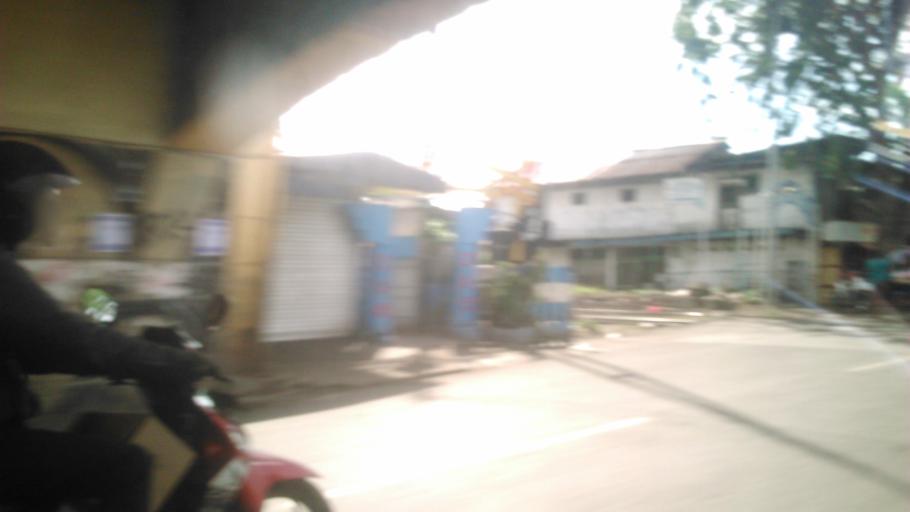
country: ID
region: East Java
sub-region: Kota Surabaya
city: Surabaya
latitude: -7.2491
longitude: 112.7531
